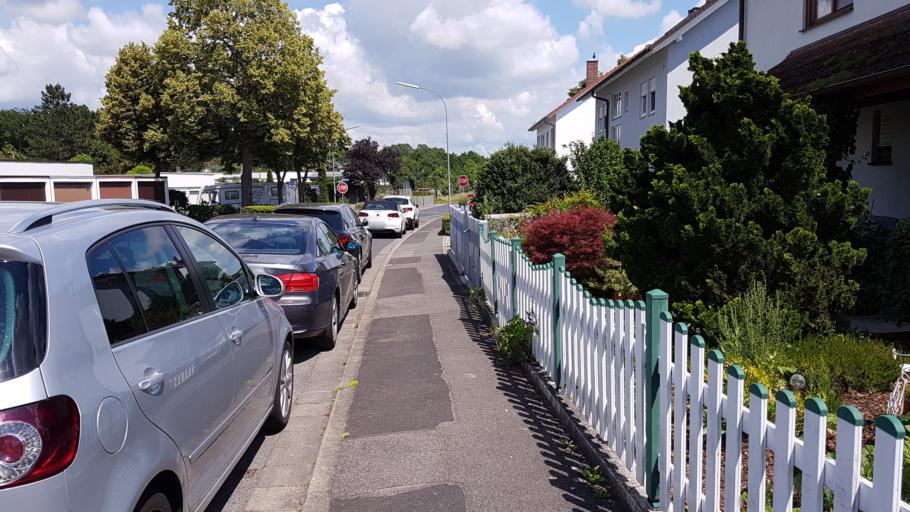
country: DE
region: Bavaria
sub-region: Regierungsbezirk Unterfranken
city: Schwebheim
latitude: 49.9968
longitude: 10.2500
